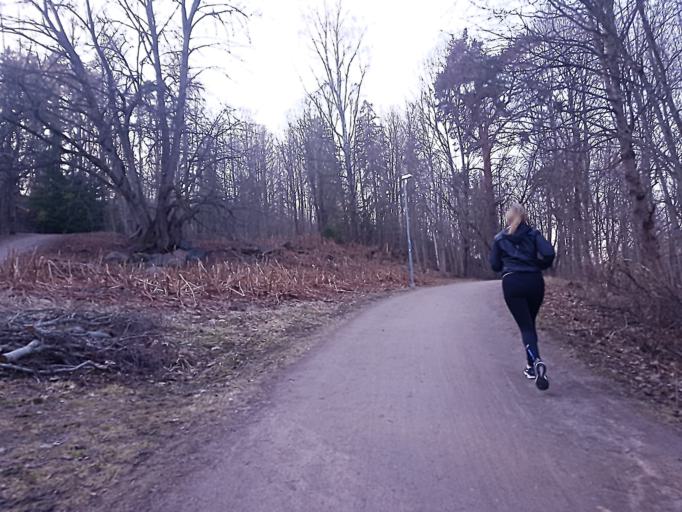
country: FI
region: Uusimaa
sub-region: Helsinki
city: Helsinki
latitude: 60.2412
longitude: 24.9720
